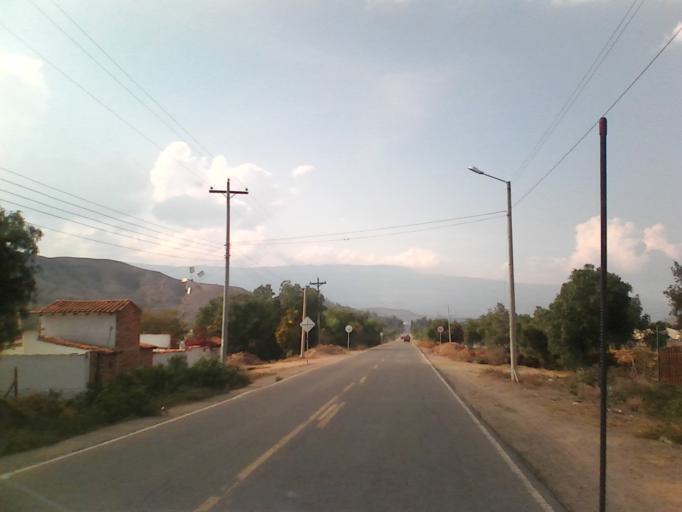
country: CO
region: Boyaca
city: Sachica
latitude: 5.5885
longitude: -73.5426
